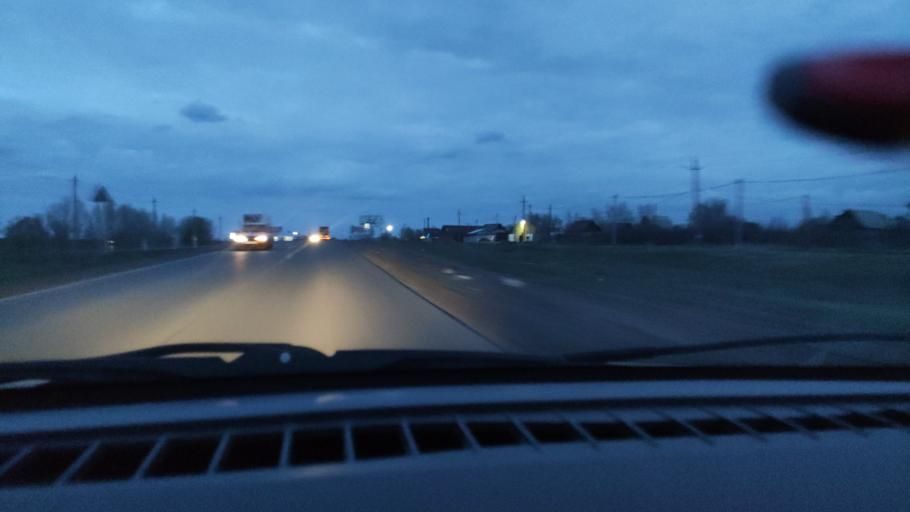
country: RU
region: Orenburg
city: Tatarskaya Kargala
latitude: 51.9014
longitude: 55.1672
